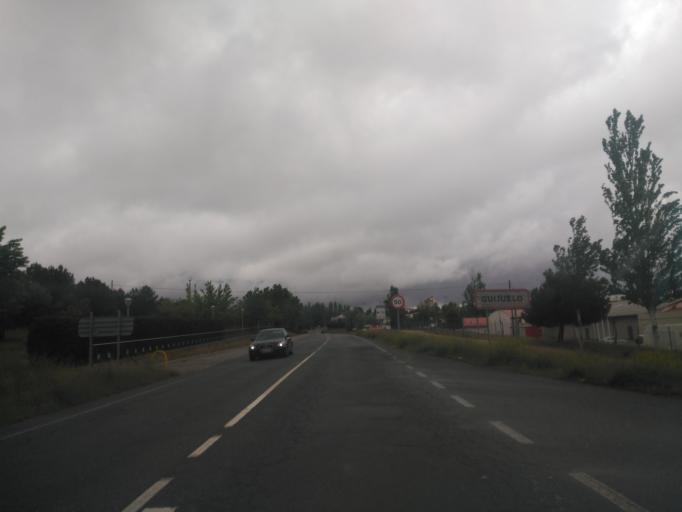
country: ES
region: Castille and Leon
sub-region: Provincia de Salamanca
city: Guijuelo
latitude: 40.5426
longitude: -5.6752
